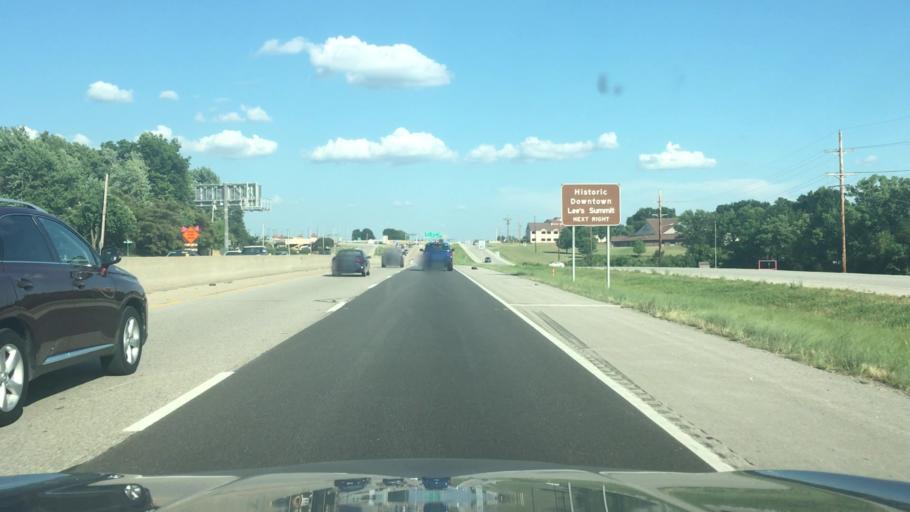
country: US
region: Missouri
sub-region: Jackson County
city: Lees Summit
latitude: 38.9070
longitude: -94.3865
